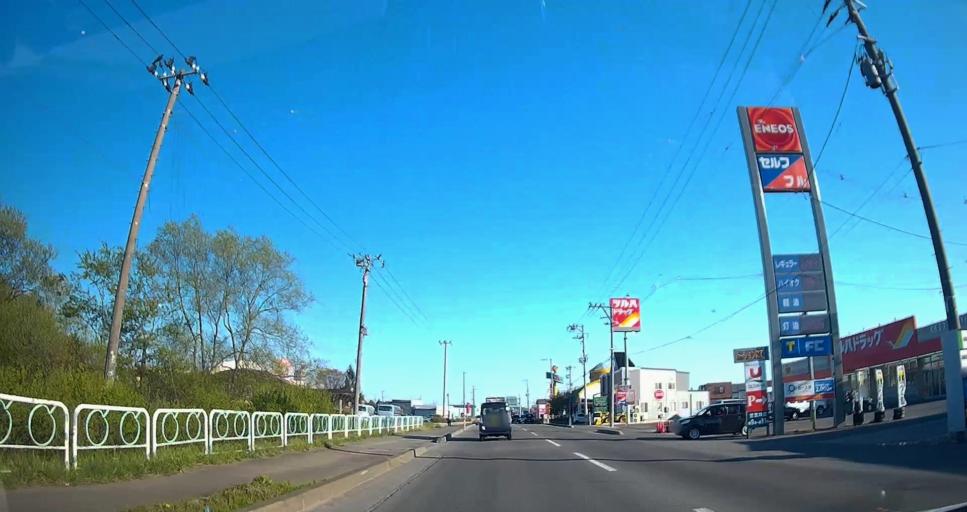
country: JP
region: Aomori
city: Mutsu
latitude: 41.3045
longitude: 141.2205
